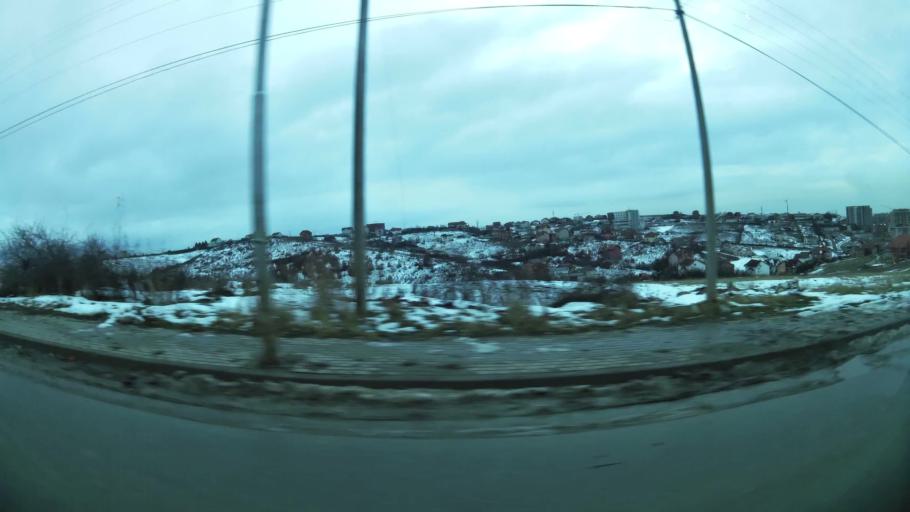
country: XK
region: Pristina
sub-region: Komuna e Prishtines
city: Pristina
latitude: 42.6344
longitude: 21.1671
